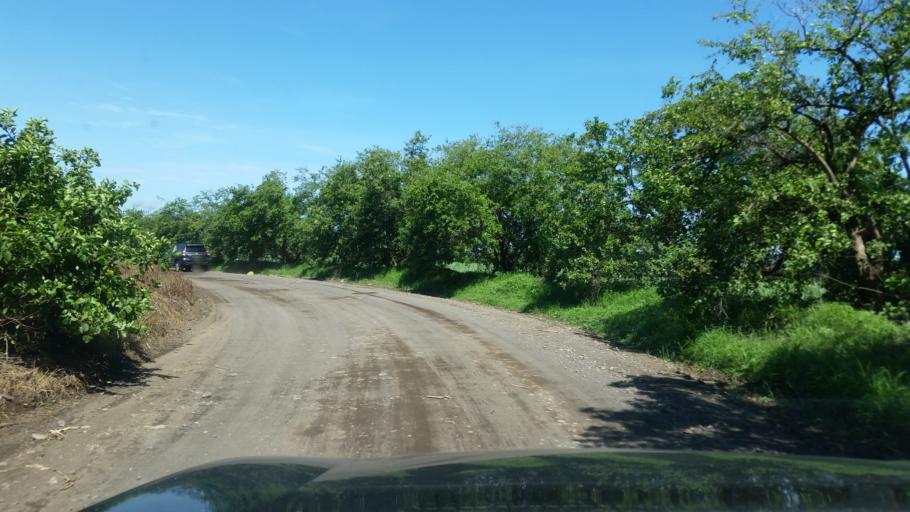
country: NI
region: Chinandega
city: Puerto Morazan
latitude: 12.7742
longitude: -87.1064
